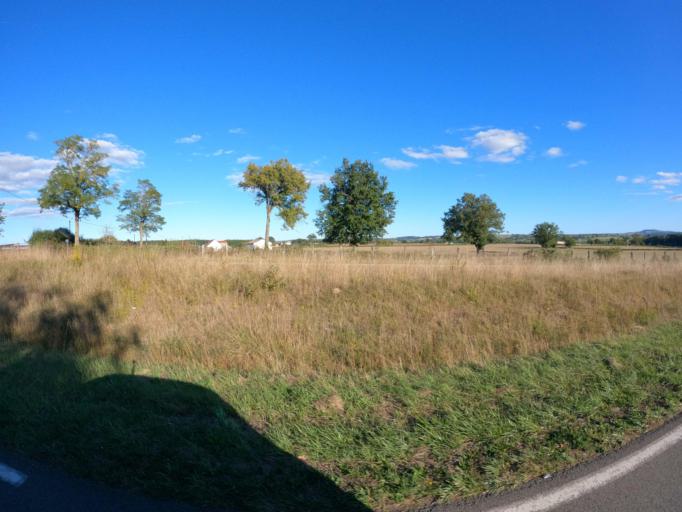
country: FR
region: Bourgogne
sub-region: Departement de Saone-et-Loire
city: Montchanin
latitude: 46.7378
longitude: 4.4446
